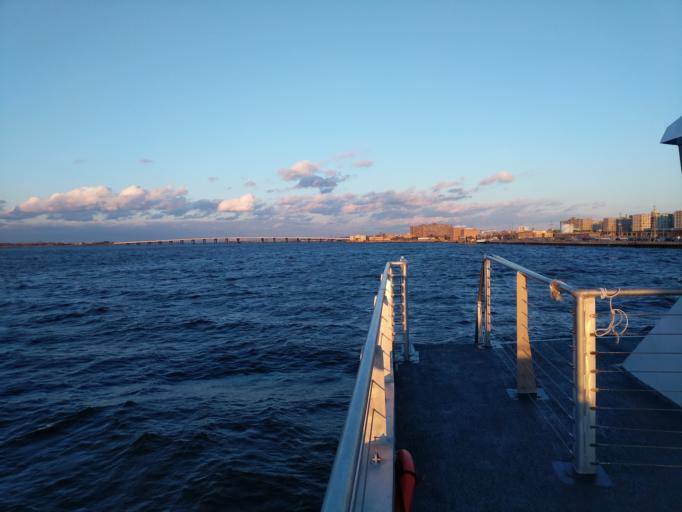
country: US
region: New York
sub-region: Kings County
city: East New York
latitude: 40.5838
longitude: -73.8375
